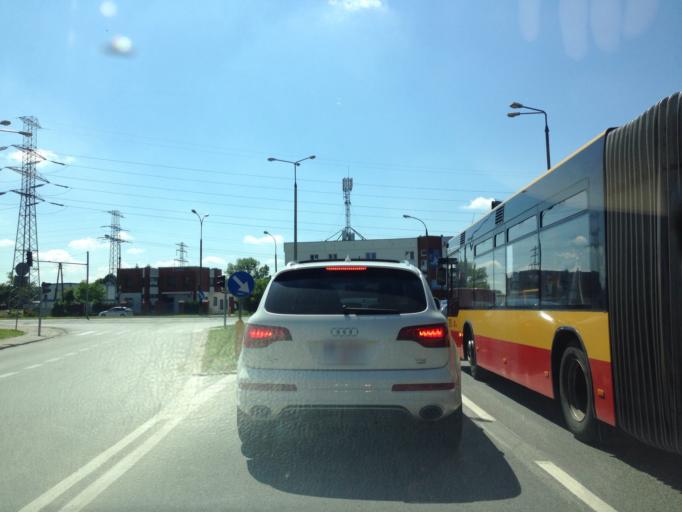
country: PL
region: Masovian Voivodeship
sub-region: Warszawa
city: Ursus
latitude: 52.2174
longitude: 20.9000
